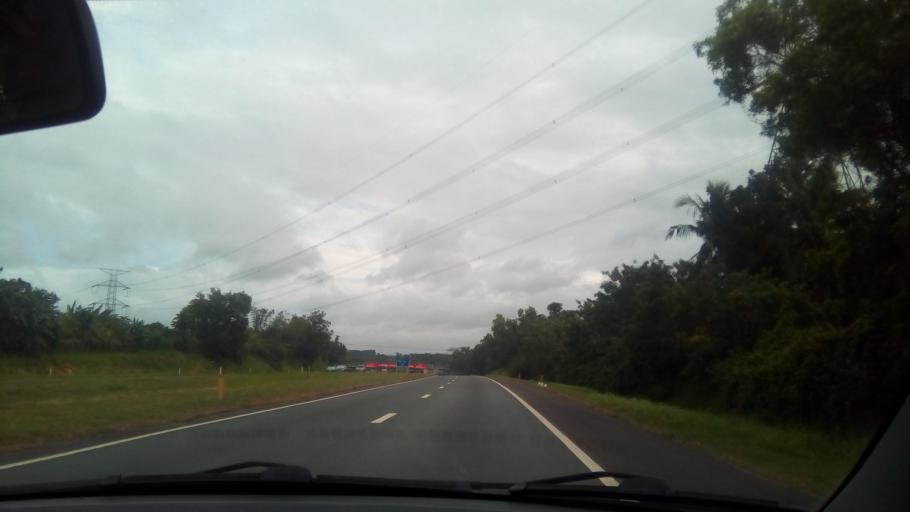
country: PH
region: Calabarzon
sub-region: Province of Batangas
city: Tanauan
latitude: 14.0734
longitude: 121.1306
